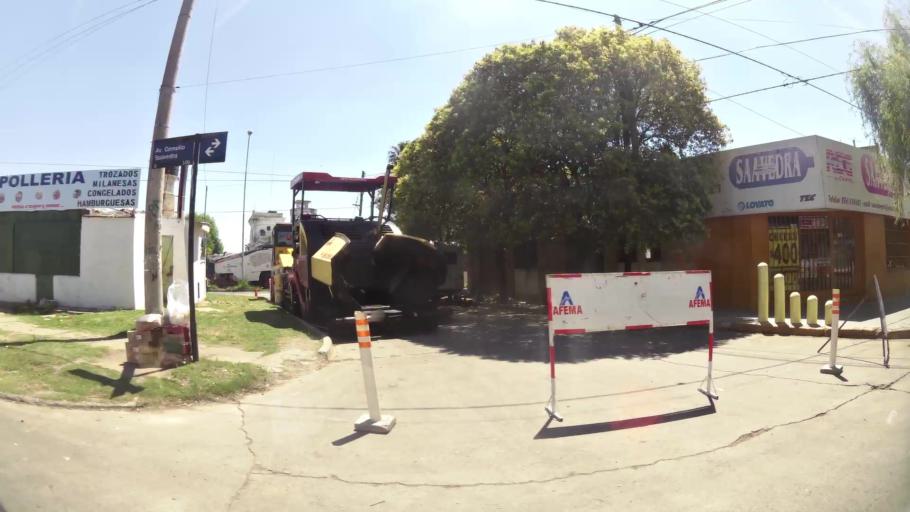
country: AR
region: Cordoba
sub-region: Departamento de Capital
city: Cordoba
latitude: -31.3910
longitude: -64.1961
